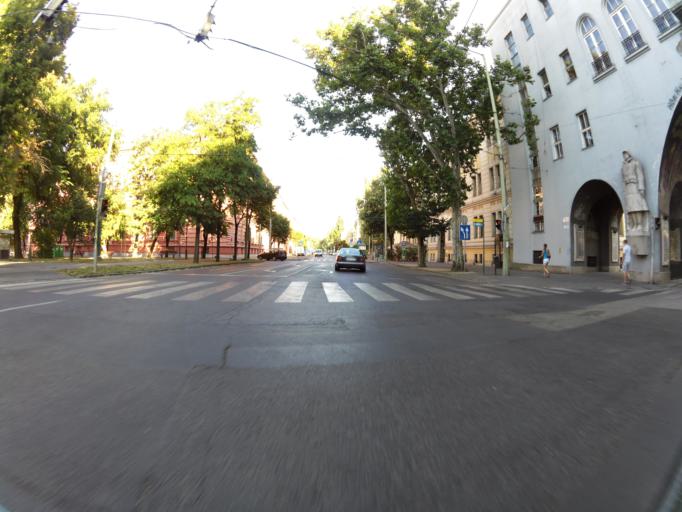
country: HU
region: Csongrad
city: Szeged
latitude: 46.2474
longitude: 20.1467
